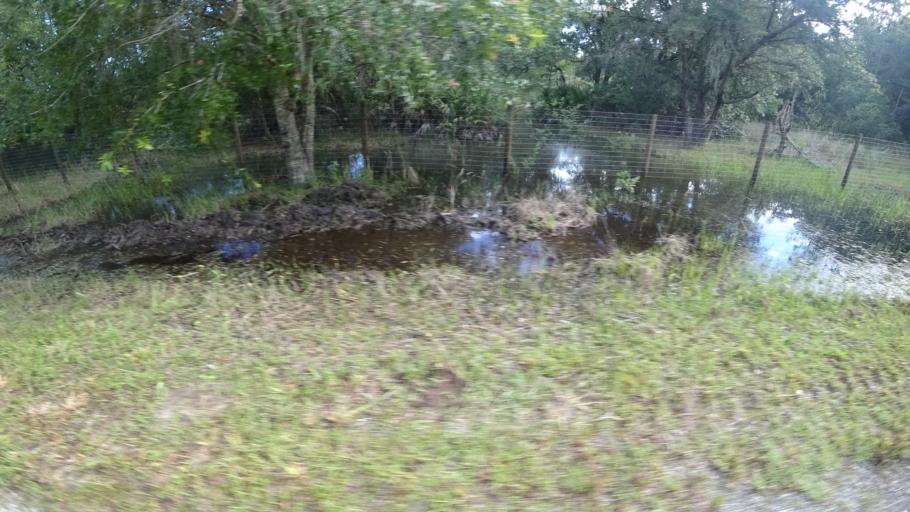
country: US
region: Florida
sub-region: Sarasota County
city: Fruitville
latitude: 27.4087
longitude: -82.2780
